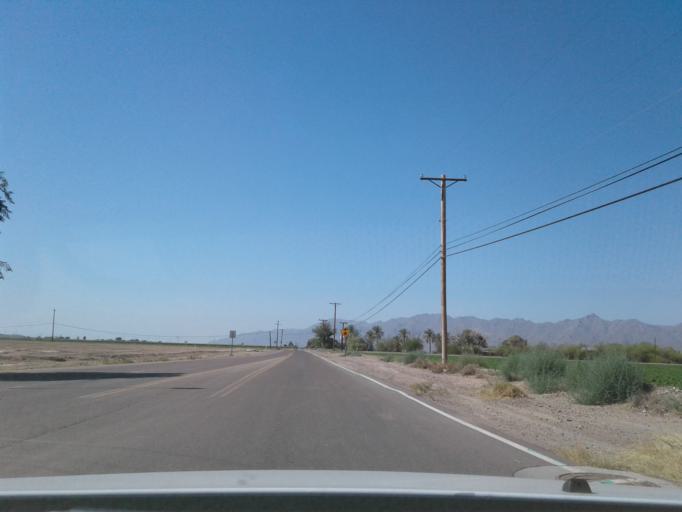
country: US
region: Arizona
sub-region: Maricopa County
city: Laveen
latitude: 33.3649
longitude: -112.1863
